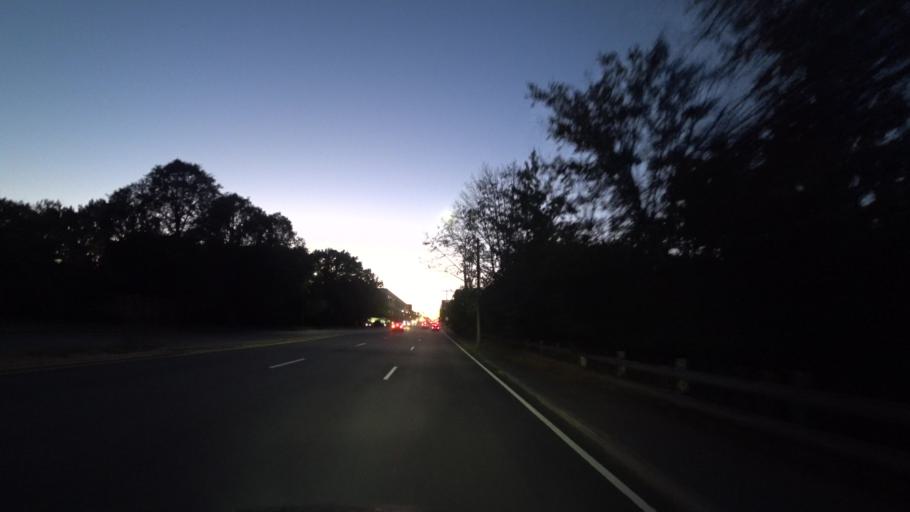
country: US
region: Massachusetts
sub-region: Middlesex County
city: Watertown
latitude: 42.3620
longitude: -71.1498
